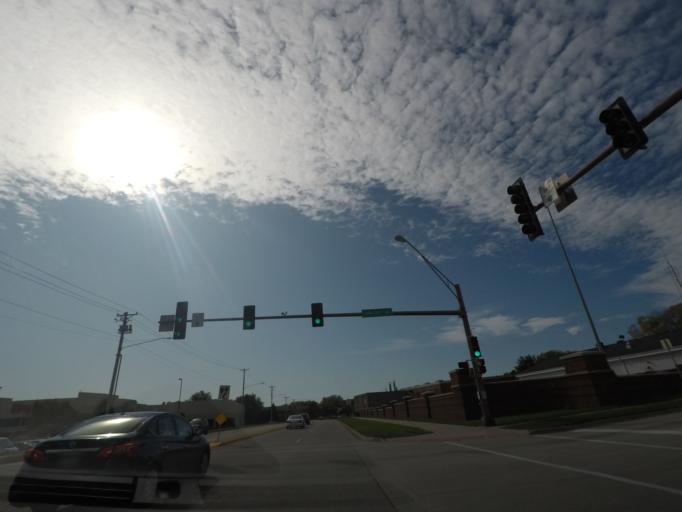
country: US
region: Iowa
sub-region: Story County
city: Ames
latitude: 42.0213
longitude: -93.6204
